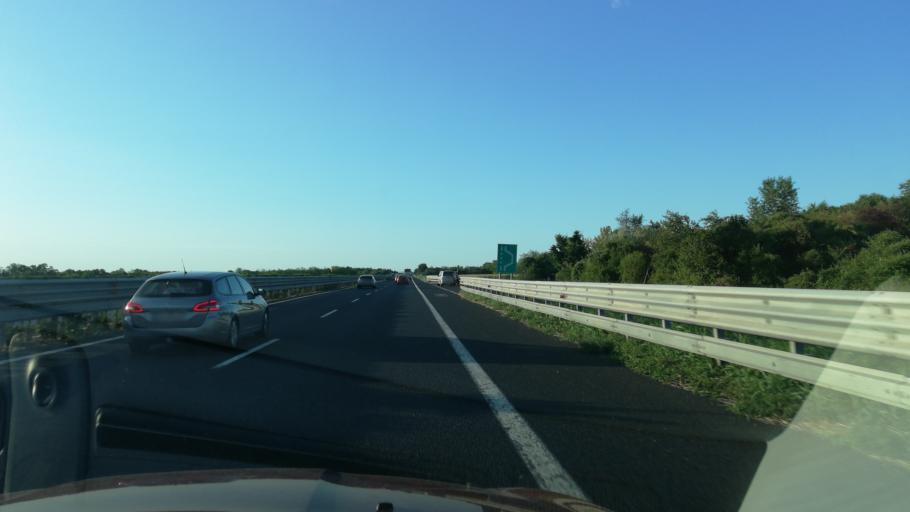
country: IT
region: Friuli Venezia Giulia
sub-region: Provincia di Udine
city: Zugliano-Terenzano-Cargnacco
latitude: 45.9983
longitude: 13.2308
